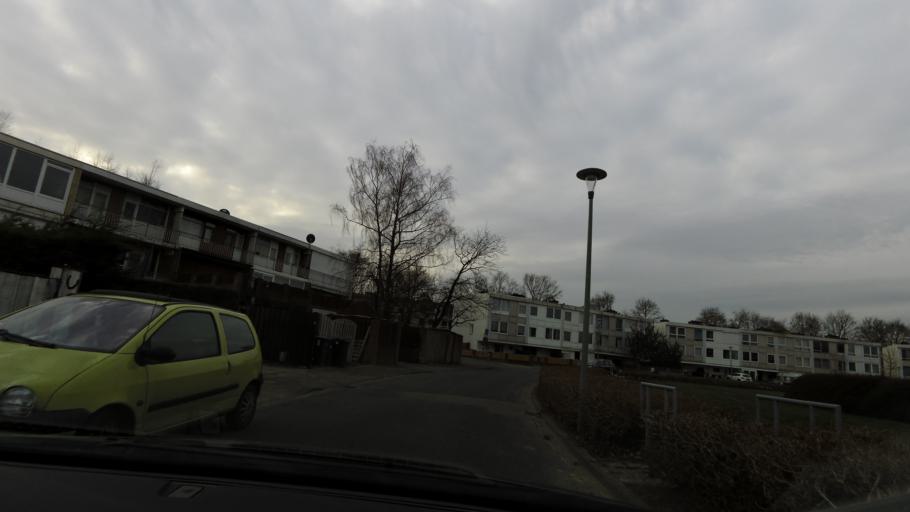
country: NL
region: Limburg
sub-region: Gemeente Brunssum
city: Brunssum
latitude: 50.9263
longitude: 5.9675
